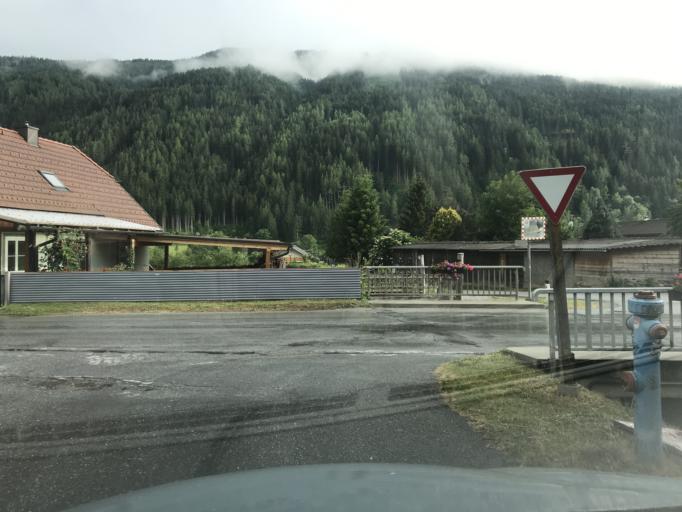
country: AT
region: Styria
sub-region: Politischer Bezirk Murau
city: Sankt Peter am Kammersberg
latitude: 47.1851
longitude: 14.1929
